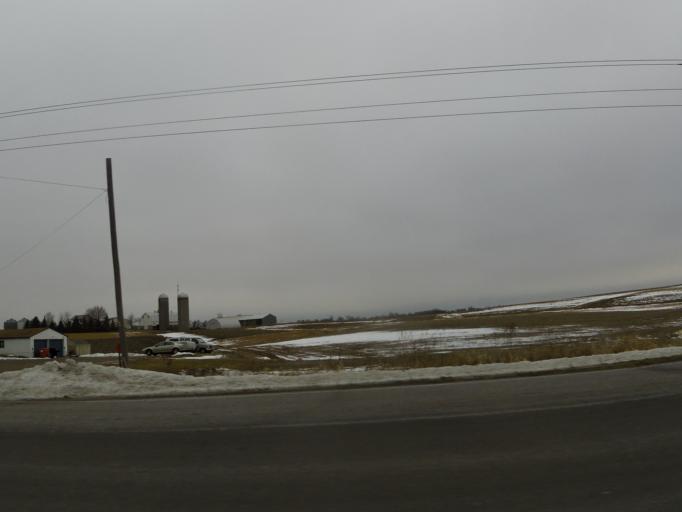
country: US
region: Minnesota
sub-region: Carver County
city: Carver
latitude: 44.7764
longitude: -93.6998
